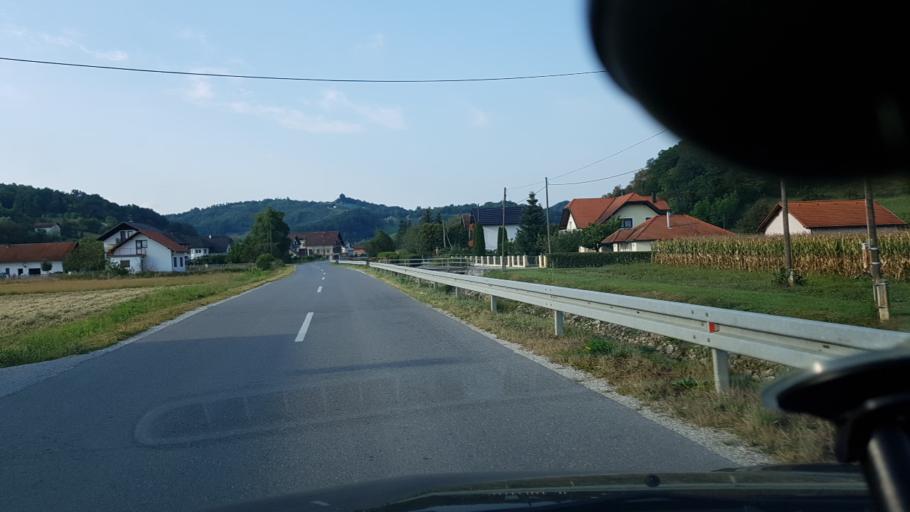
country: SI
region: Podcetrtek
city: Podcetrtek
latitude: 46.1378
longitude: 15.6669
